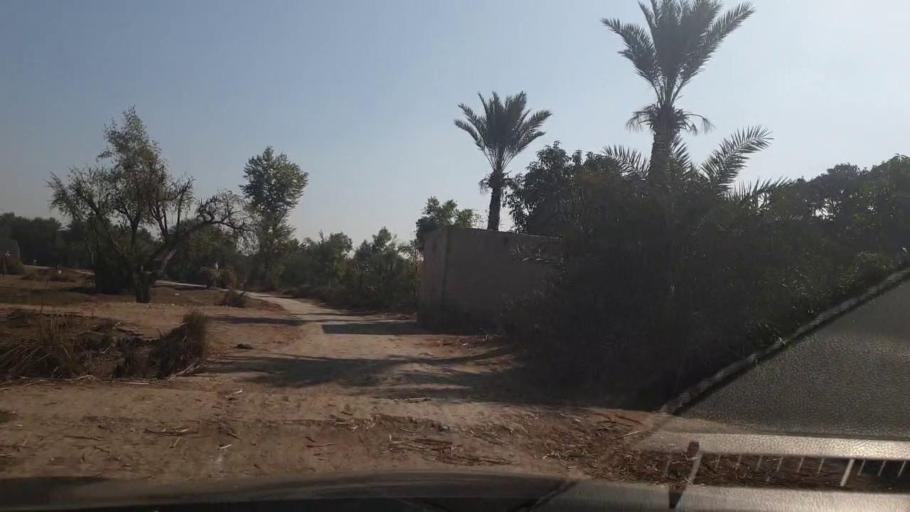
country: PK
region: Sindh
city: Ubauro
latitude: 28.1456
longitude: 69.6927
